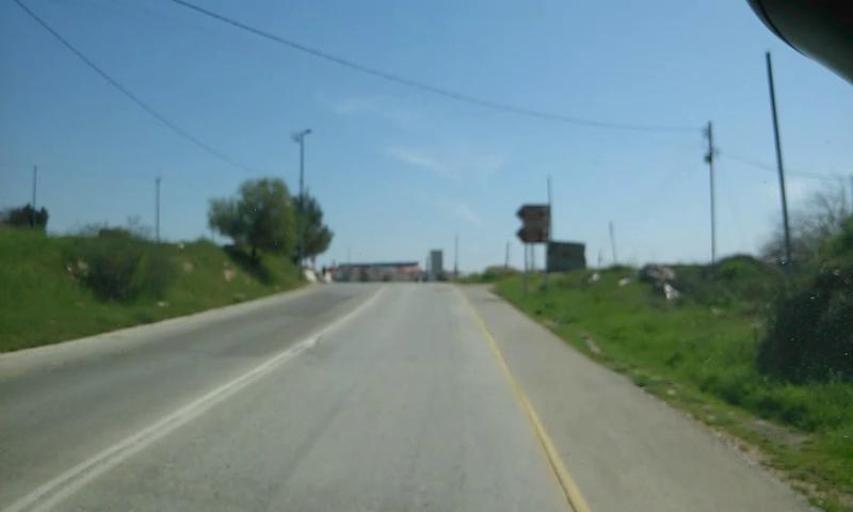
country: PS
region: West Bank
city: Nahhalin
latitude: 31.6547
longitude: 35.1221
